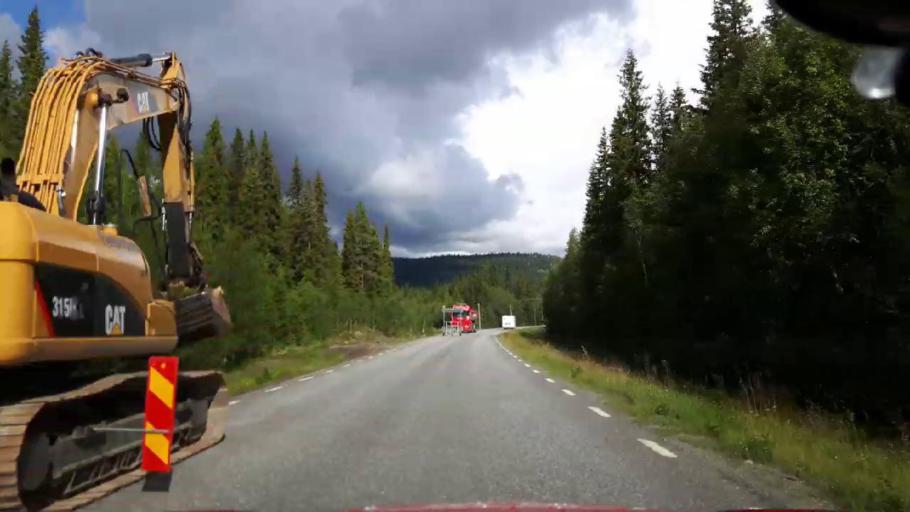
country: SE
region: Vaesterbotten
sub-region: Vilhelmina Kommun
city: Sjoberg
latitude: 64.9321
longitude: 15.8594
